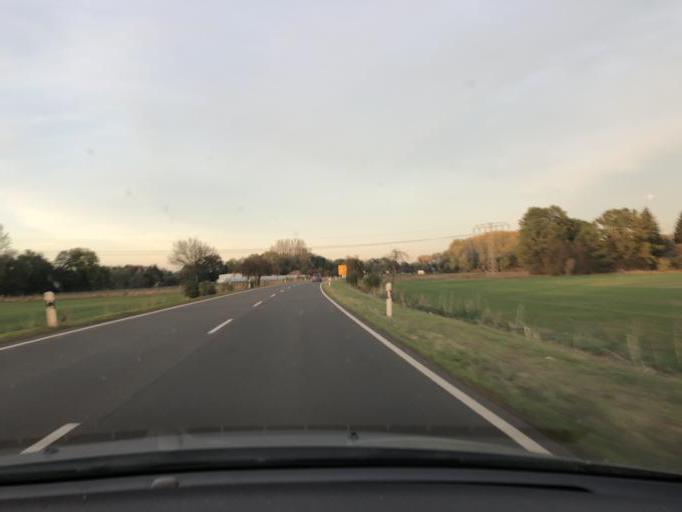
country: DE
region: Saxony
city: Pegau
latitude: 51.1567
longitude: 12.2499
